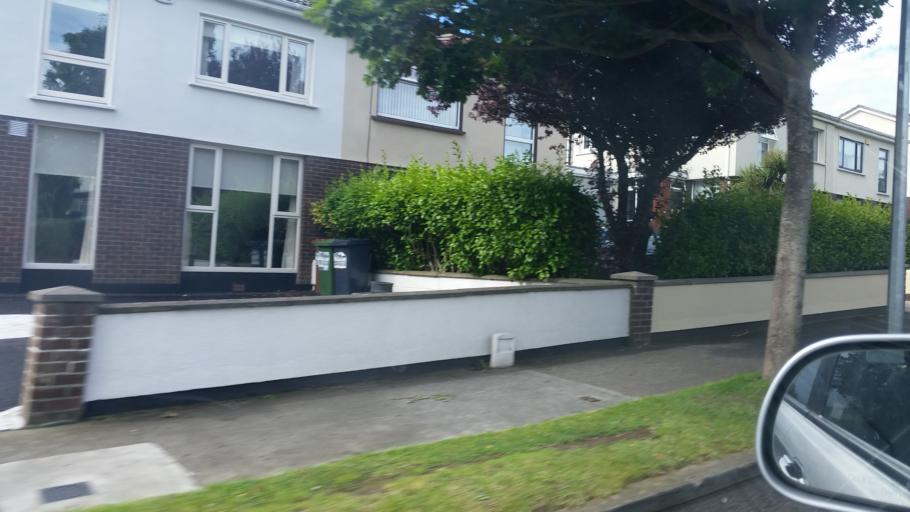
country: IE
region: Leinster
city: Portmarnock
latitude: 53.4342
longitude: -6.1277
